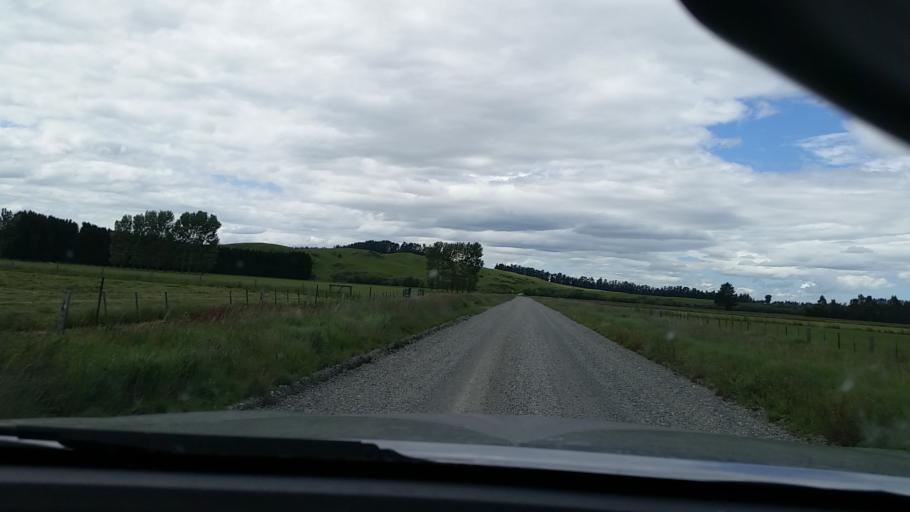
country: NZ
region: Otago
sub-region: Queenstown-Lakes District
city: Kingston
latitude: -45.7753
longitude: 168.6188
